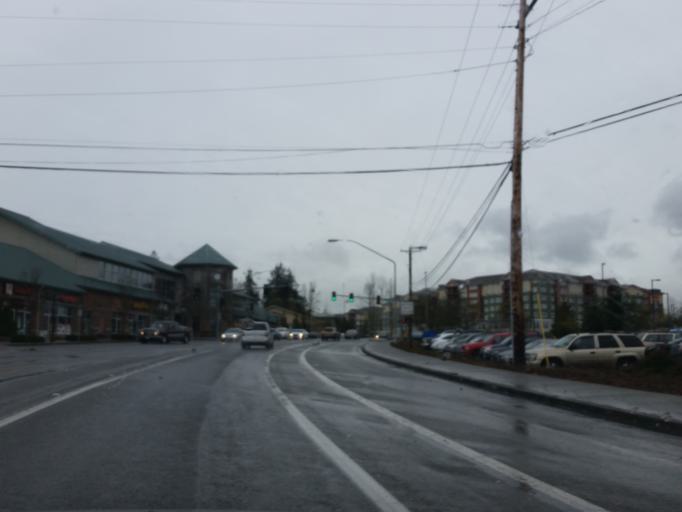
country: US
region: Washington
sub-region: Snohomish County
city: Martha Lake
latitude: 47.8521
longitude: -122.2603
